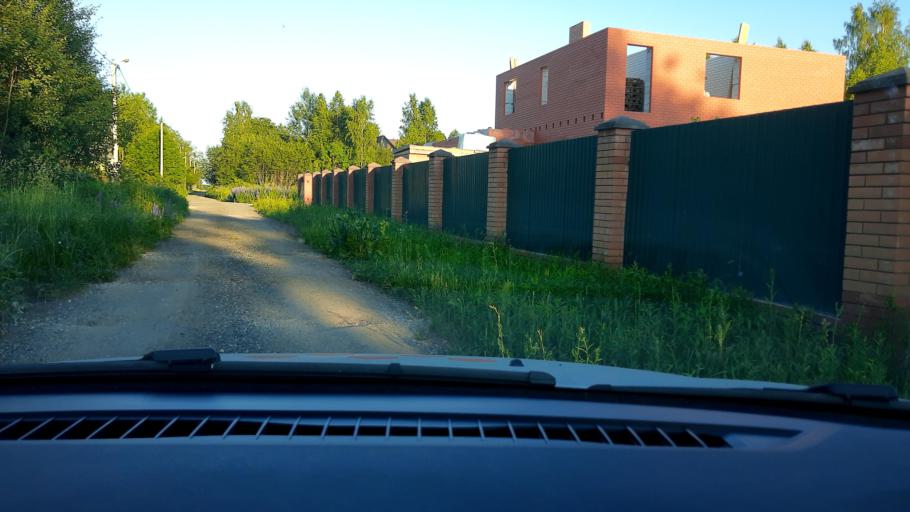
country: RU
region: Nizjnij Novgorod
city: Kstovo
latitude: 56.3081
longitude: 44.2741
